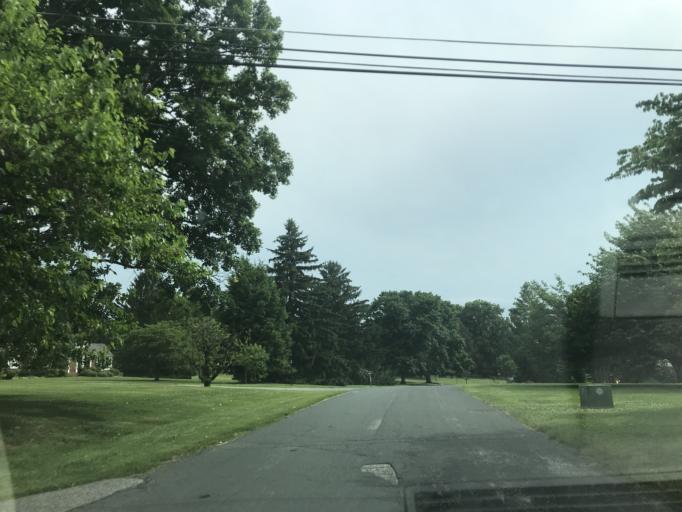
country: US
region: Maryland
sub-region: Baltimore County
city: Hampton
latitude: 39.4242
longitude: -76.5900
